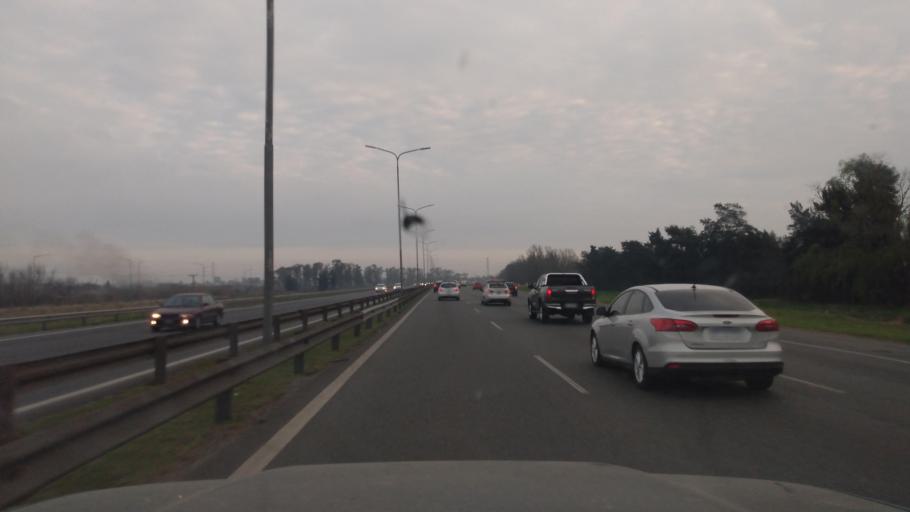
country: AR
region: Buenos Aires
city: Hurlingham
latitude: -34.5427
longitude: -58.6018
